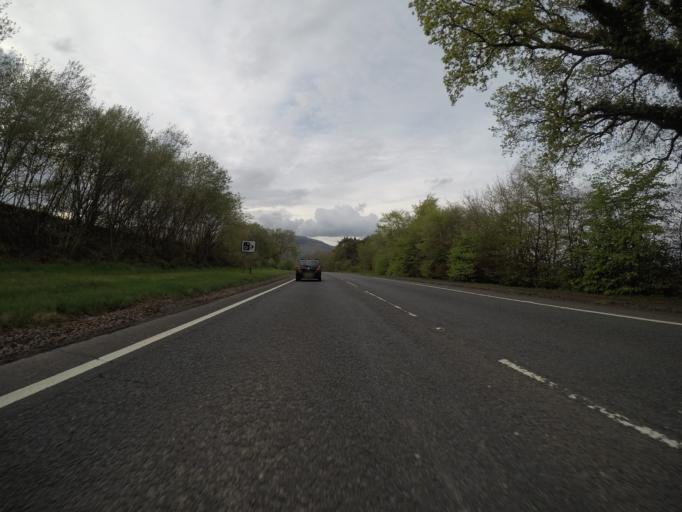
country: GB
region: Scotland
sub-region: West Dunbartonshire
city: Balloch
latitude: 56.0309
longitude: -4.6353
